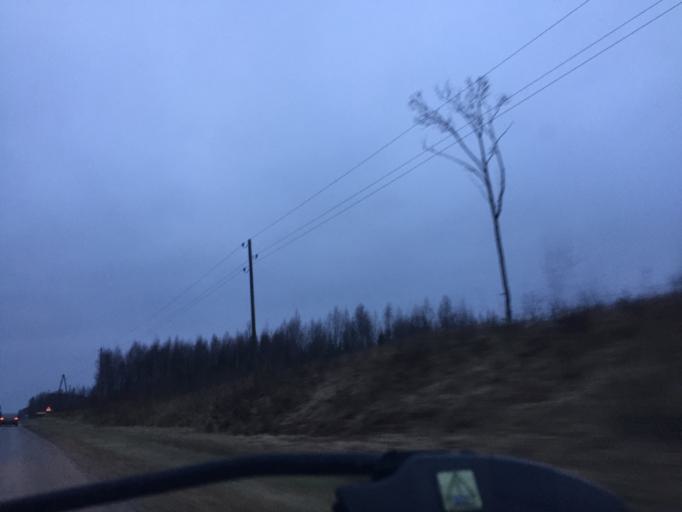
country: LV
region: Limbazu Rajons
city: Limbazi
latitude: 57.6038
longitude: 24.8076
